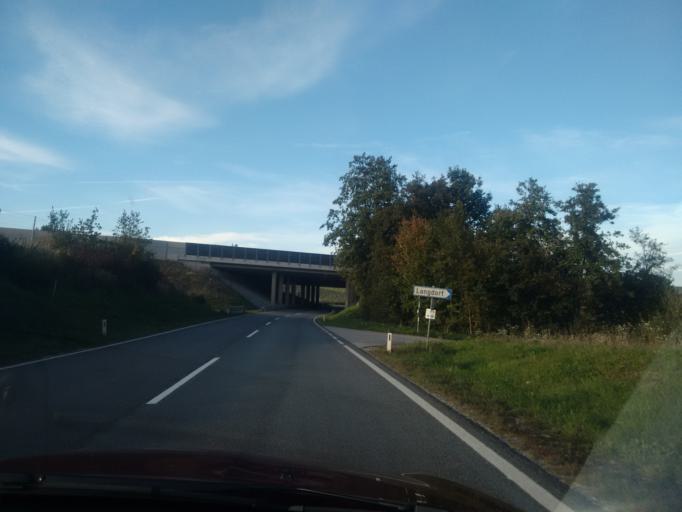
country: AT
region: Upper Austria
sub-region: Wels-Land
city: Offenhausen
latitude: 48.1783
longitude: 13.7772
